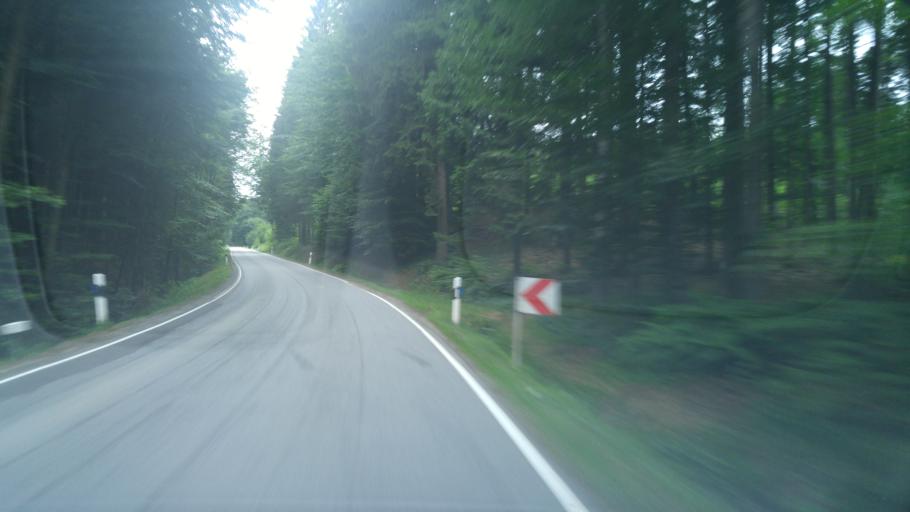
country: DE
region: Baden-Wuerttemberg
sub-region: Regierungsbezirk Stuttgart
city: Wustenrot
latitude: 49.0922
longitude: 9.4724
